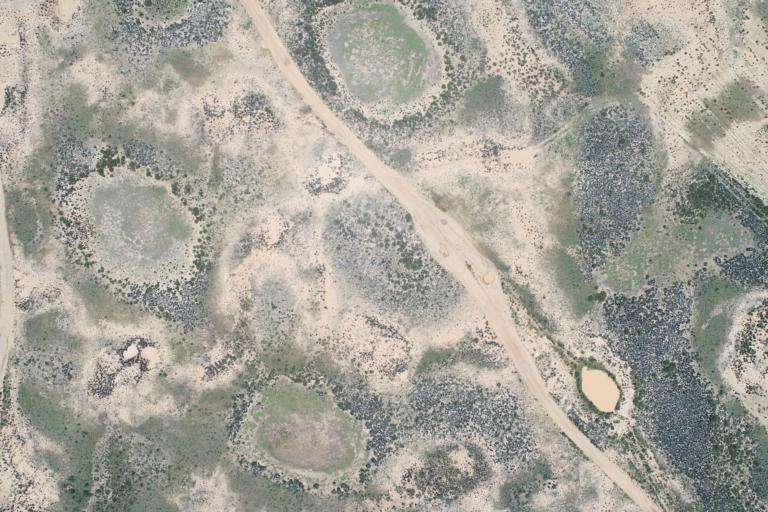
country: BO
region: La Paz
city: Patacamaya
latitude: -17.2815
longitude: -68.5040
